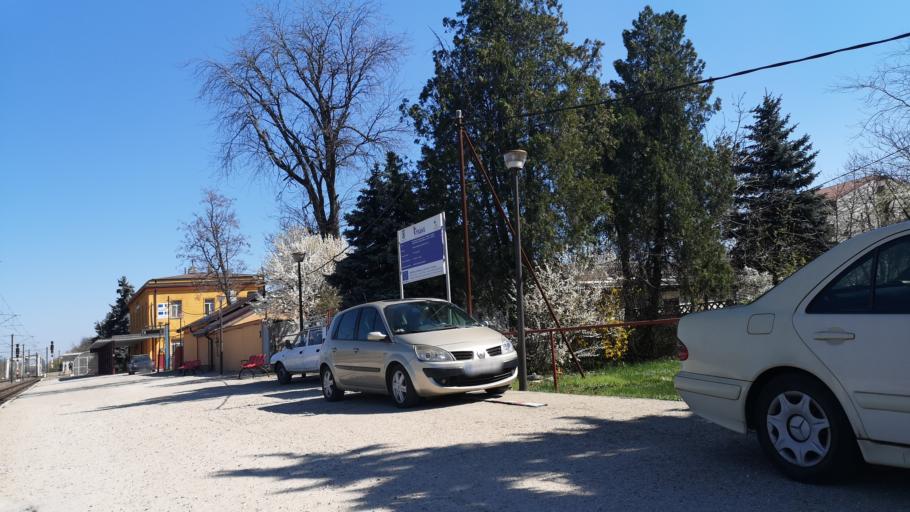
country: RO
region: Bucuresti
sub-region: Municipiul Bucuresti
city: Bucuresti
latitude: 44.4850
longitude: 26.0729
